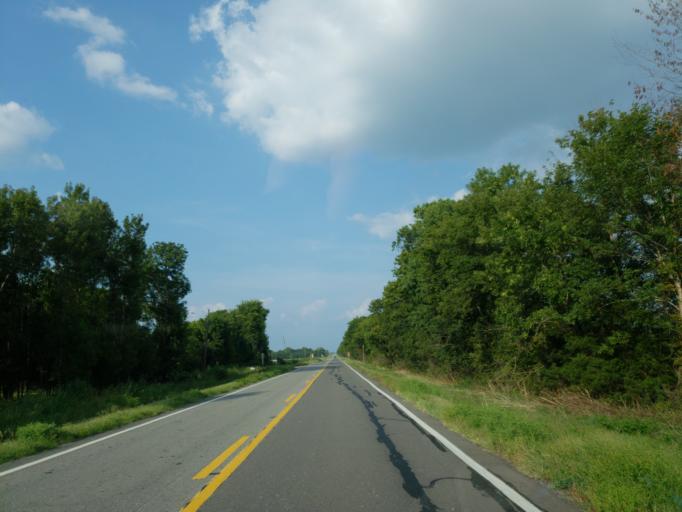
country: US
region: Alabama
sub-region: Greene County
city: Eutaw
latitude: 32.7941
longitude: -87.9696
